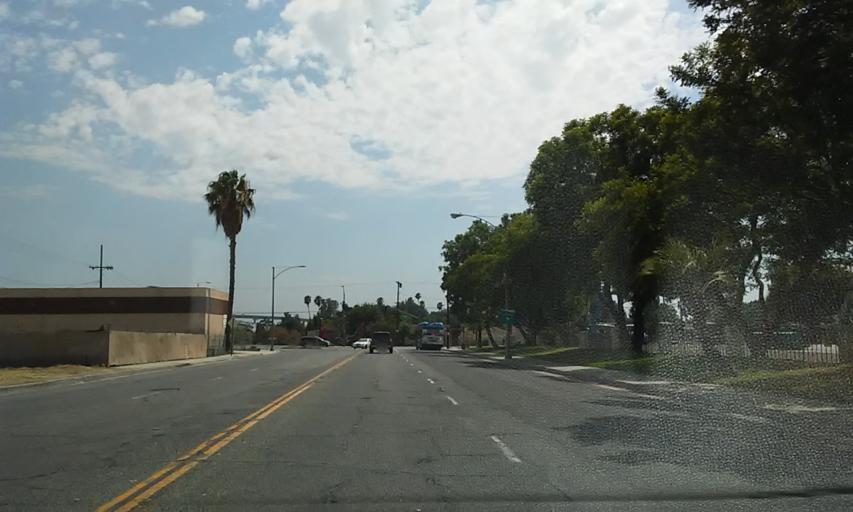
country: US
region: California
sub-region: Riverside County
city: Highgrove
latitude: 34.0030
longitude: -117.3530
